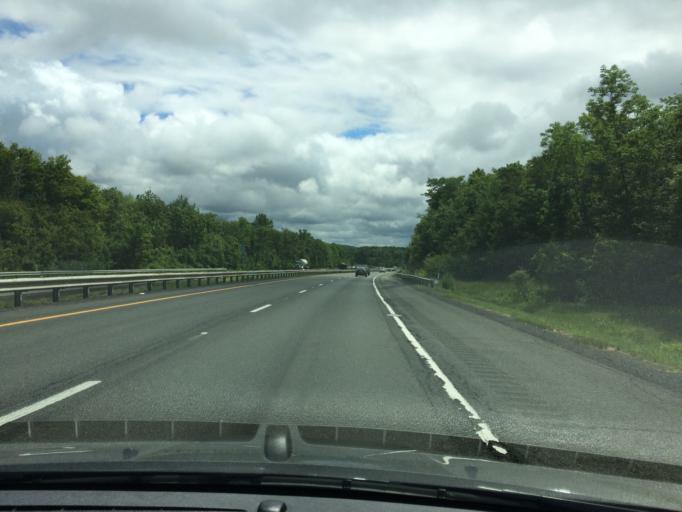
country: US
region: Massachusetts
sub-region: Berkshire County
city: Otis
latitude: 42.2431
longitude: -73.0715
